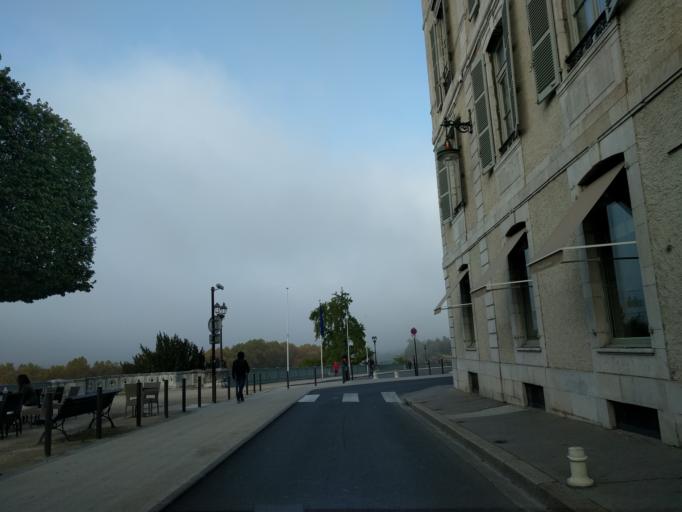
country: FR
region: Aquitaine
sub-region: Departement des Pyrenees-Atlantiques
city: Pau
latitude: 43.2935
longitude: -0.3719
